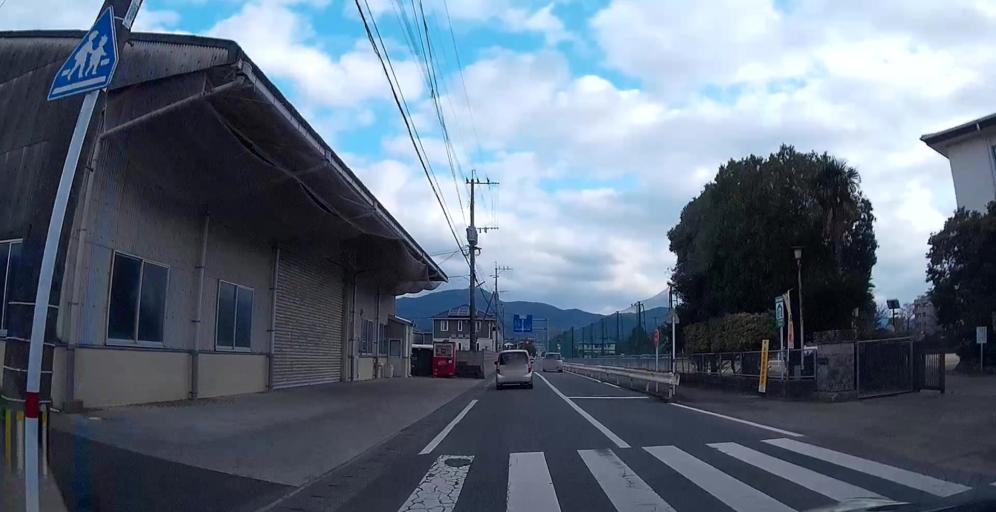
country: JP
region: Kumamoto
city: Yatsushiro
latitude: 32.5371
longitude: 130.6312
